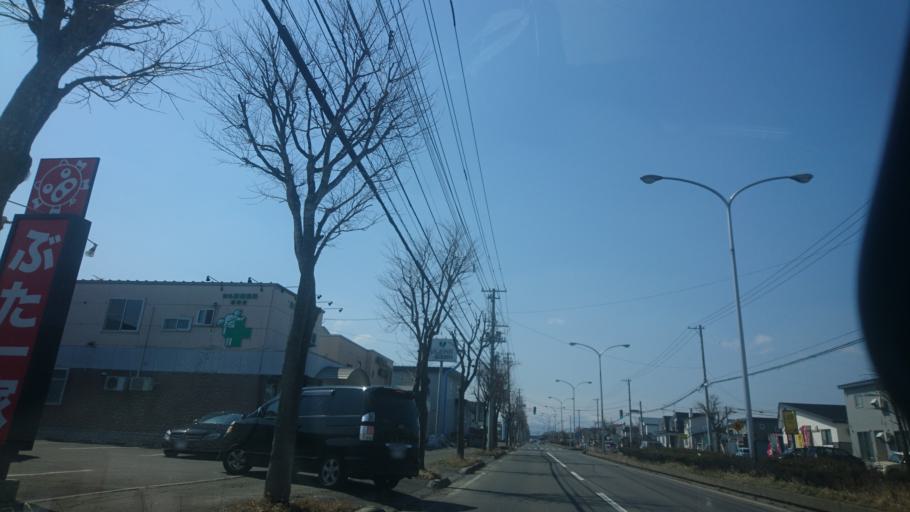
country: JP
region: Hokkaido
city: Obihiro
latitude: 42.9161
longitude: 143.1225
